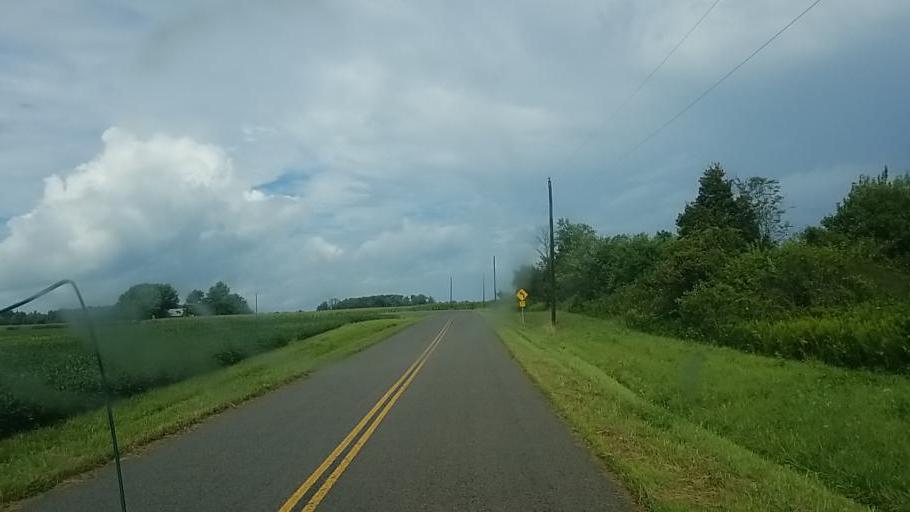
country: US
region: Ohio
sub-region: Hardin County
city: Kenton
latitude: 40.4691
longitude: -83.5107
